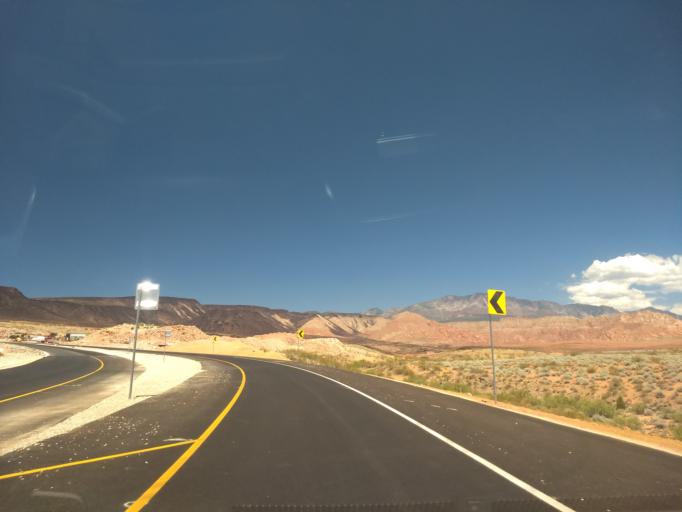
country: US
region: Utah
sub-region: Washington County
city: Washington
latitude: 37.1580
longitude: -113.5195
